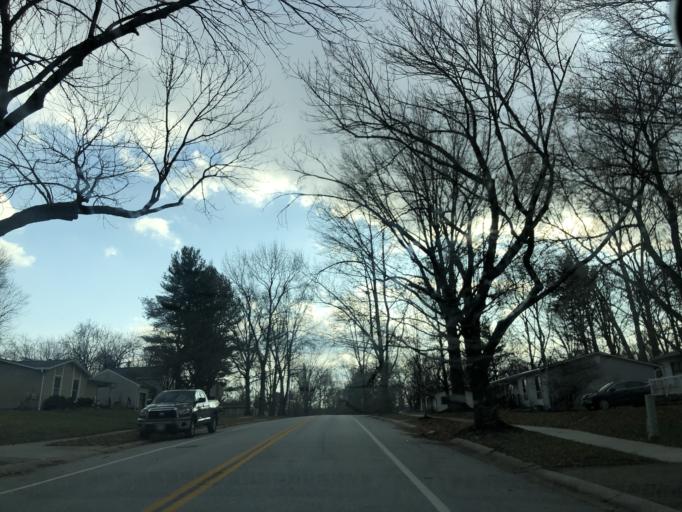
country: US
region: Maryland
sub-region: Howard County
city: Columbia
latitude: 39.2018
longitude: -76.8389
